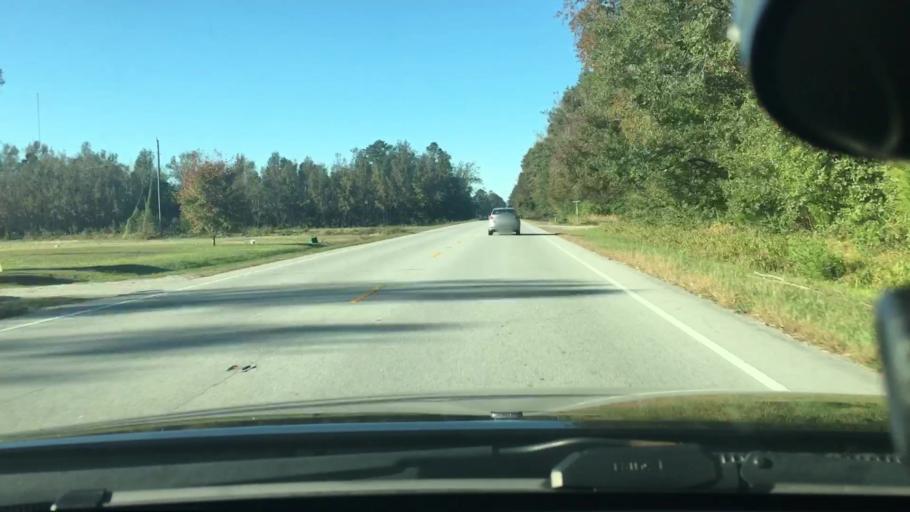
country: US
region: North Carolina
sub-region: Craven County
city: New Bern
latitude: 35.1710
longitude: -77.0432
